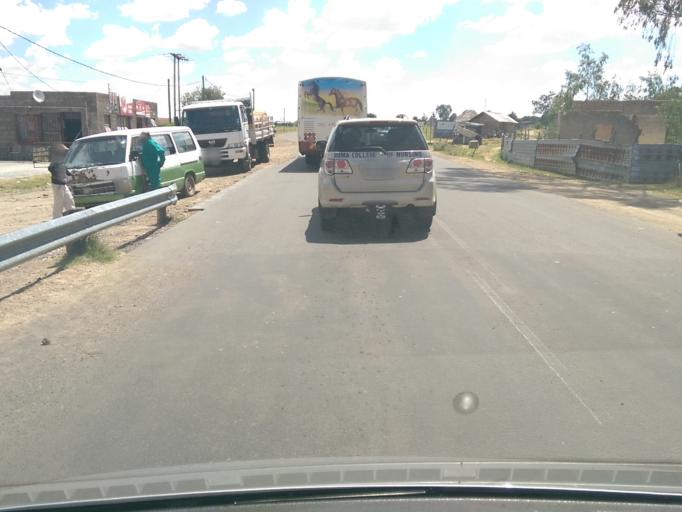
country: LS
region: Maseru
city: Maseru
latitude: -29.4110
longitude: 27.6195
